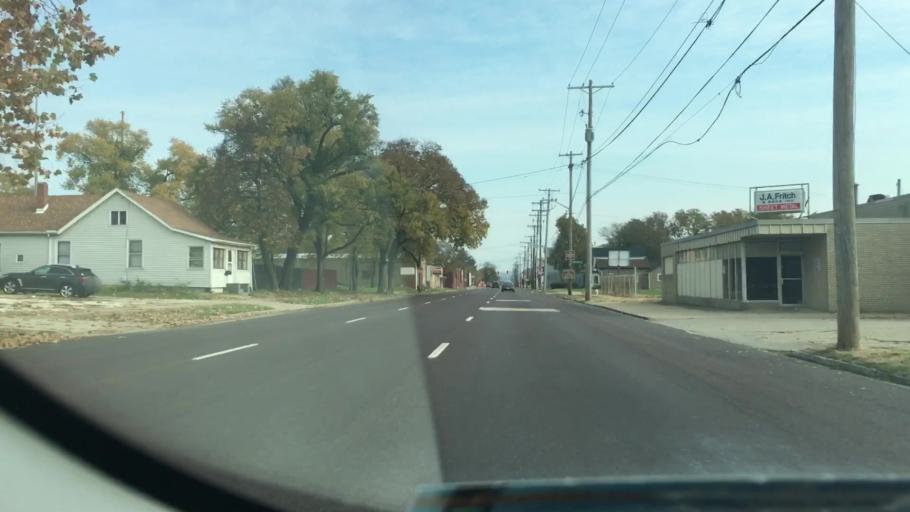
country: US
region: Illinois
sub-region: Peoria County
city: Peoria
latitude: 40.6990
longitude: -89.5782
